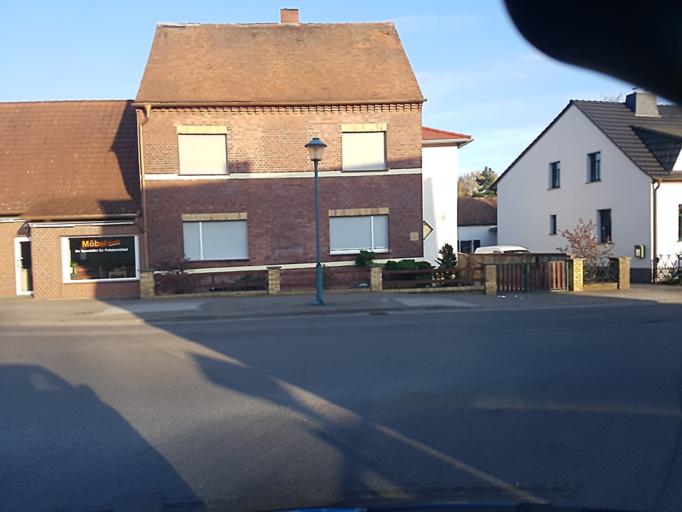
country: DE
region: Saxony
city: Bad Duben
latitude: 51.5933
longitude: 12.5916
